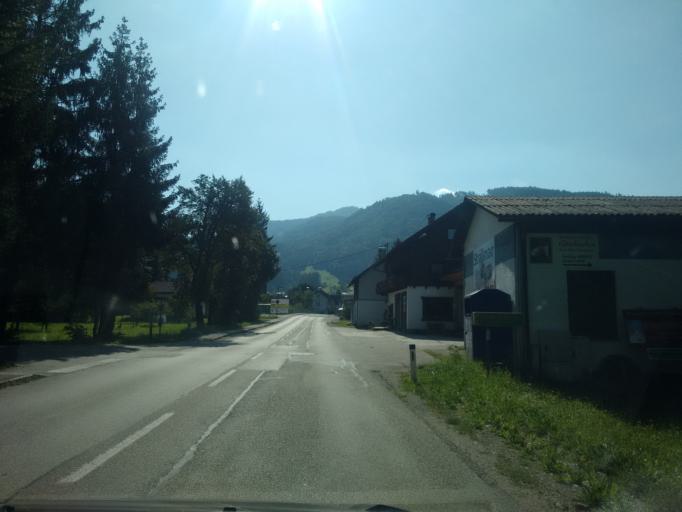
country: AT
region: Upper Austria
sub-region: Politischer Bezirk Gmunden
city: Gruenau im Almtal
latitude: 47.8572
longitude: 13.9546
